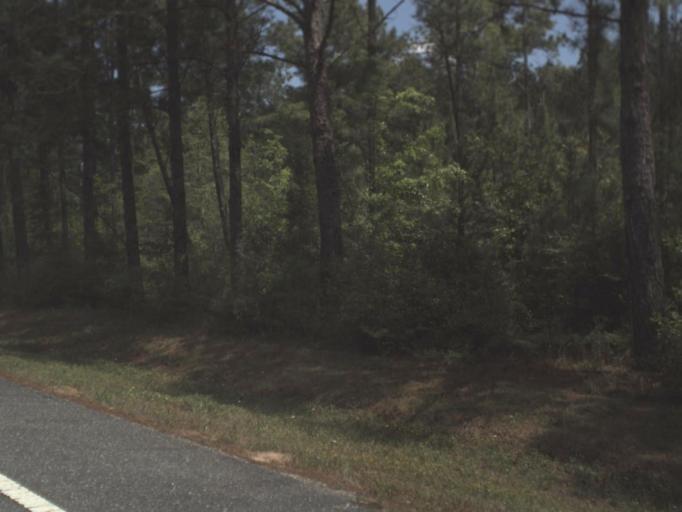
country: US
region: Alabama
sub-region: Escambia County
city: East Brewton
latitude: 30.9015
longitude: -87.0381
